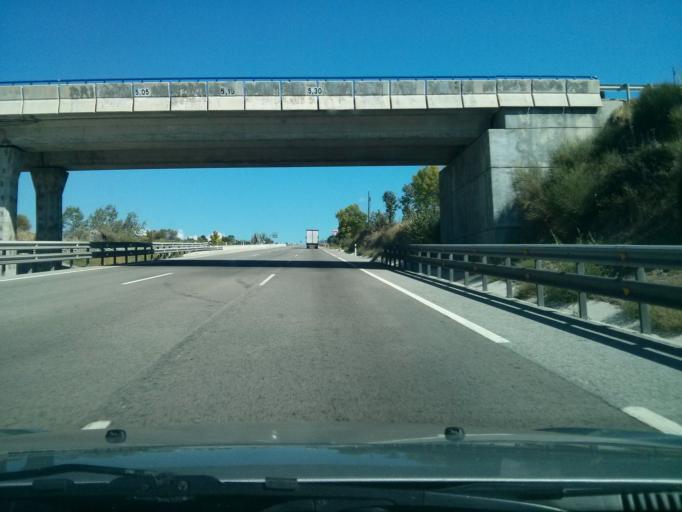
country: ES
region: Madrid
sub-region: Provincia de Madrid
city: Gascones
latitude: 41.0277
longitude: -3.6223
